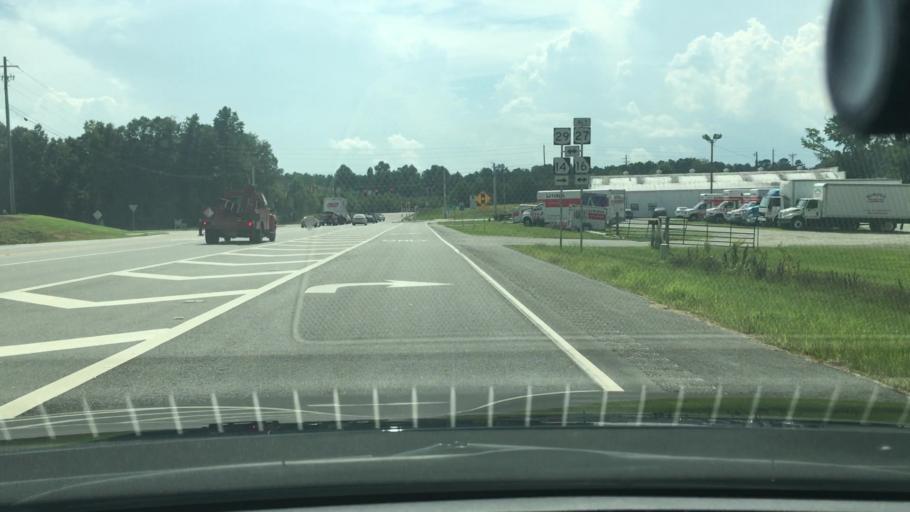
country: US
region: Georgia
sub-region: Coweta County
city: East Newnan
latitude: 33.3300
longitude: -84.7790
